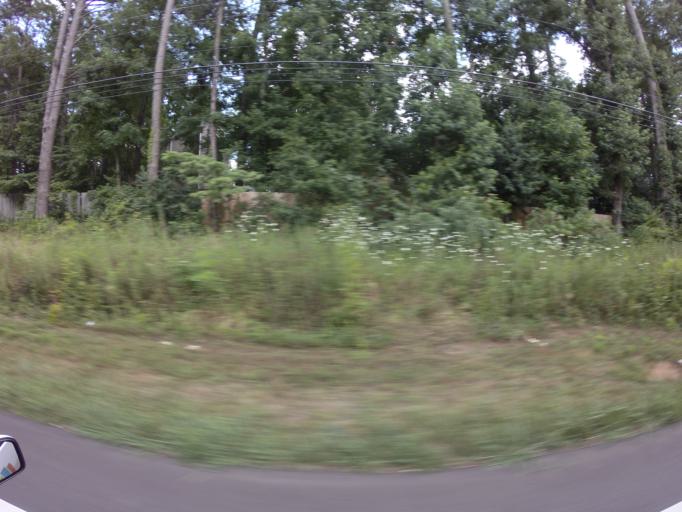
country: US
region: Georgia
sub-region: Fulton County
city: Alpharetta
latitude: 34.0203
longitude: -84.2813
